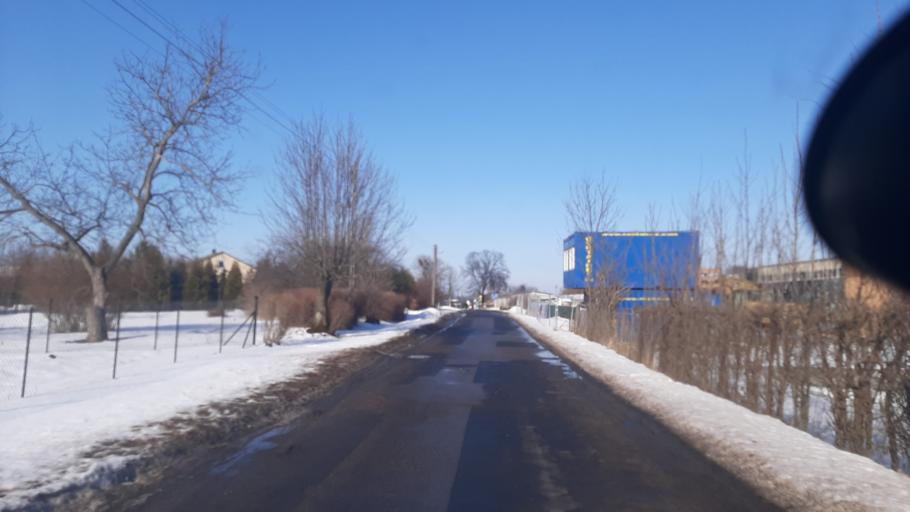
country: PL
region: Lublin Voivodeship
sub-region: Powiat lubelski
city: Wojciechow
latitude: 51.2861
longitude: 22.2833
